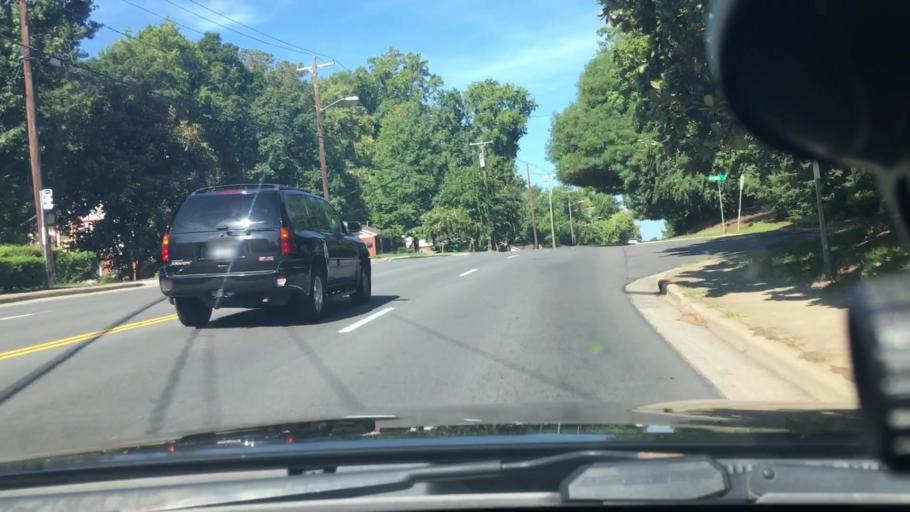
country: US
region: North Carolina
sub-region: Mecklenburg County
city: Matthews
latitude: 35.1857
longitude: -80.7391
